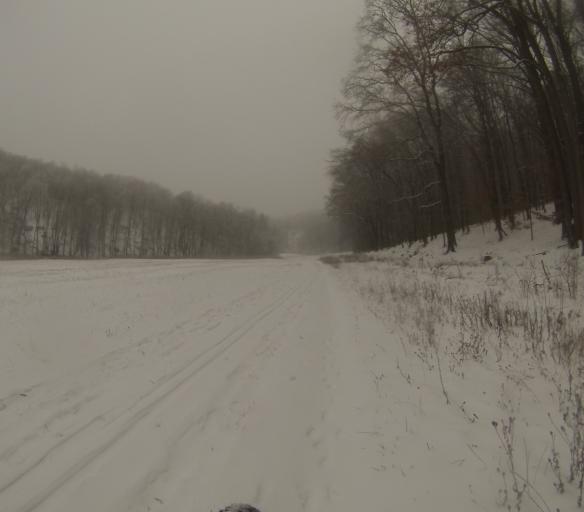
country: CZ
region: South Moravian
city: Strelice
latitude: 49.1343
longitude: 16.5023
